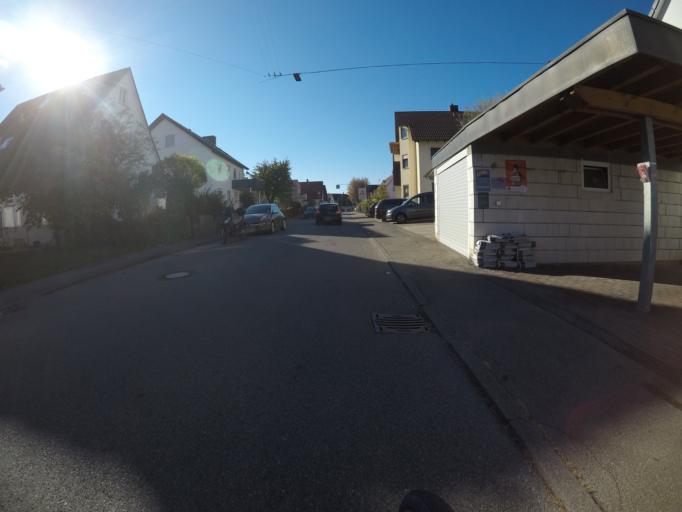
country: DE
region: Baden-Wuerttemberg
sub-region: Regierungsbezirk Stuttgart
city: Filderstadt
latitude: 48.6536
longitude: 9.2198
